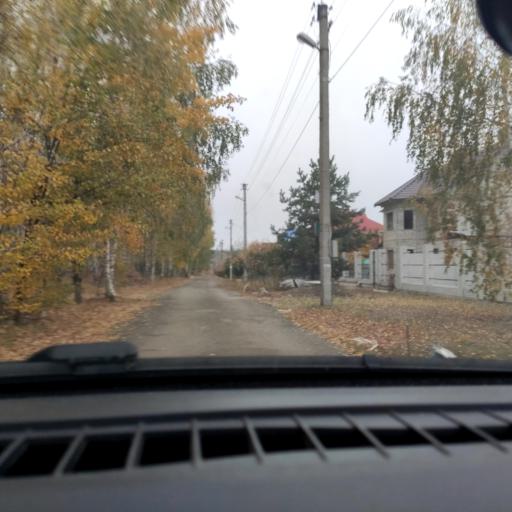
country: RU
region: Voronezj
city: Podgornoye
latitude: 51.7655
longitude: 39.1850
